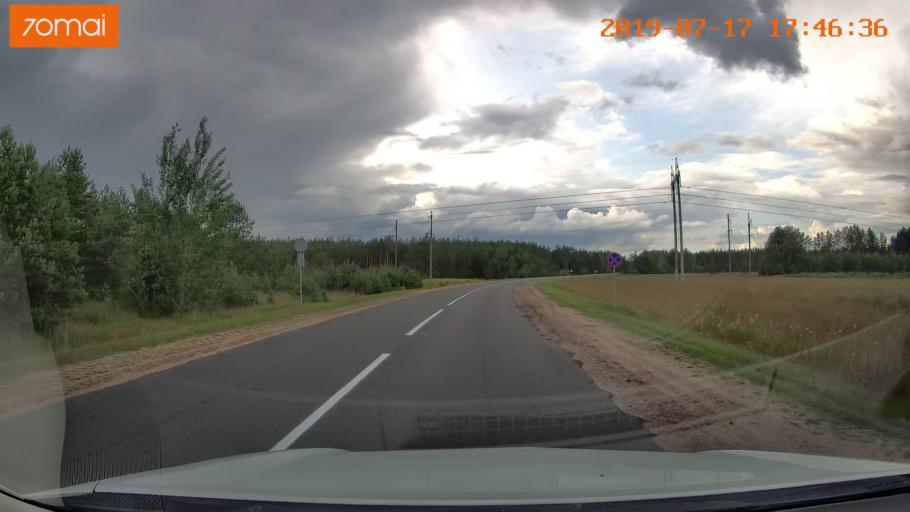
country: BY
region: Mogilev
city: Hlusha
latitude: 53.0999
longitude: 28.8374
